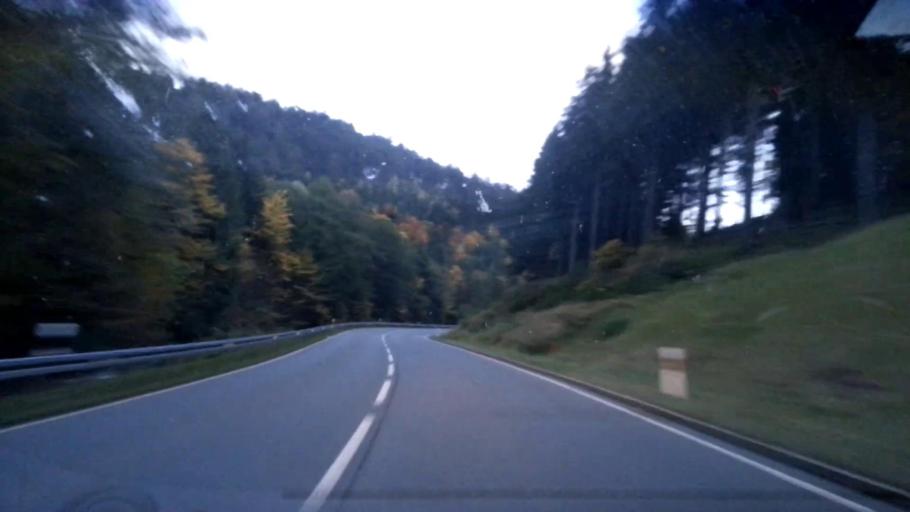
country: DE
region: Bavaria
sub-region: Upper Franconia
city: Warmensteinach
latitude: 49.9823
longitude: 11.7670
